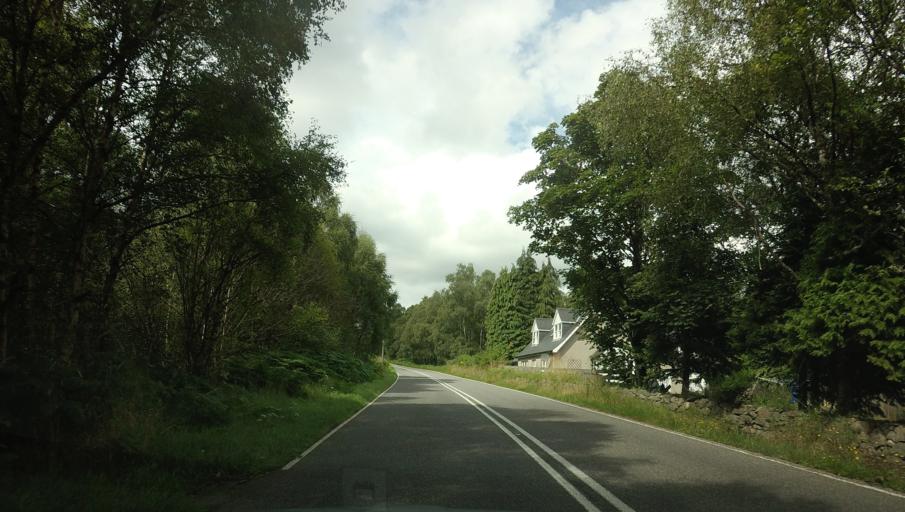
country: GB
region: Scotland
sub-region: Aberdeenshire
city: Torphins
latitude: 57.0641
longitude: -2.5772
